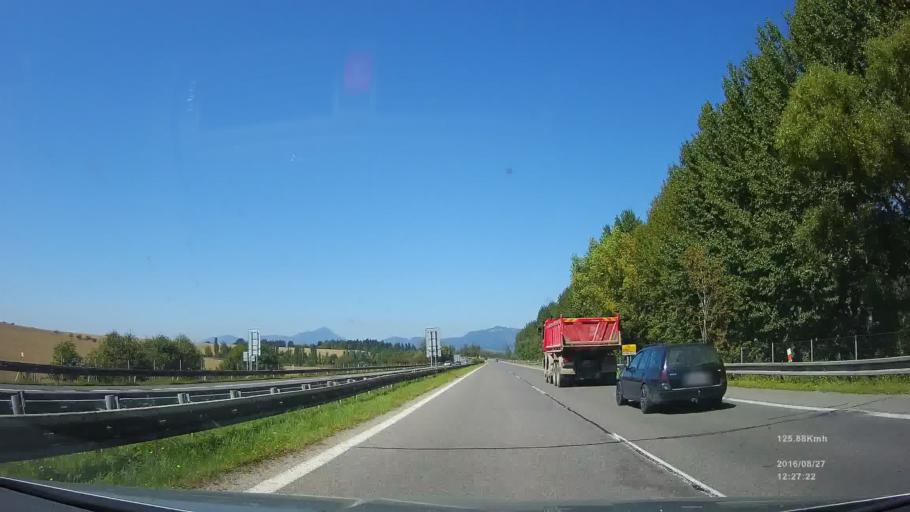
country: SK
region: Zilinsky
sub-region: Okres Liptovsky Mikulas
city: Liptovsky Mikulas
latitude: 49.0784
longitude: 19.5904
